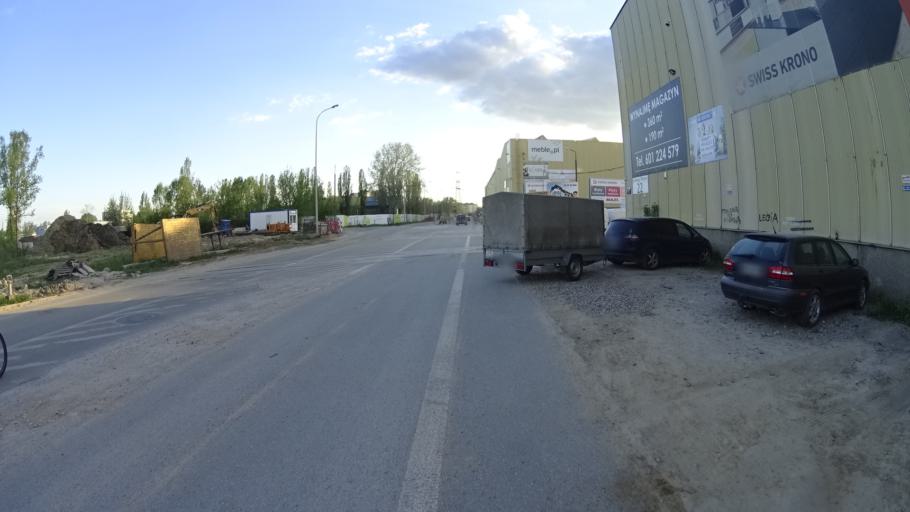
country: PL
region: Masovian Voivodeship
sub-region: Warszawa
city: Ursus
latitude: 52.2035
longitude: 20.8777
